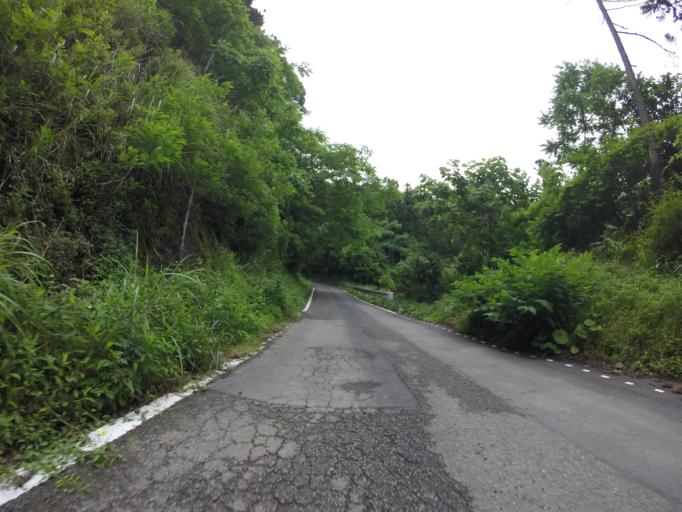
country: JP
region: Shizuoka
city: Shizuoka-shi
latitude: 35.0457
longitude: 138.3108
